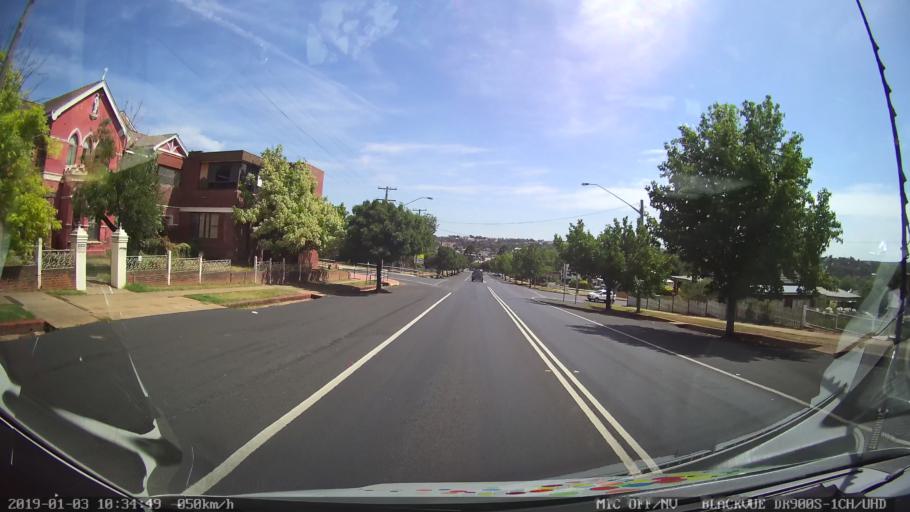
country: AU
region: New South Wales
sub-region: Young
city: Young
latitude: -34.3193
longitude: 148.2923
